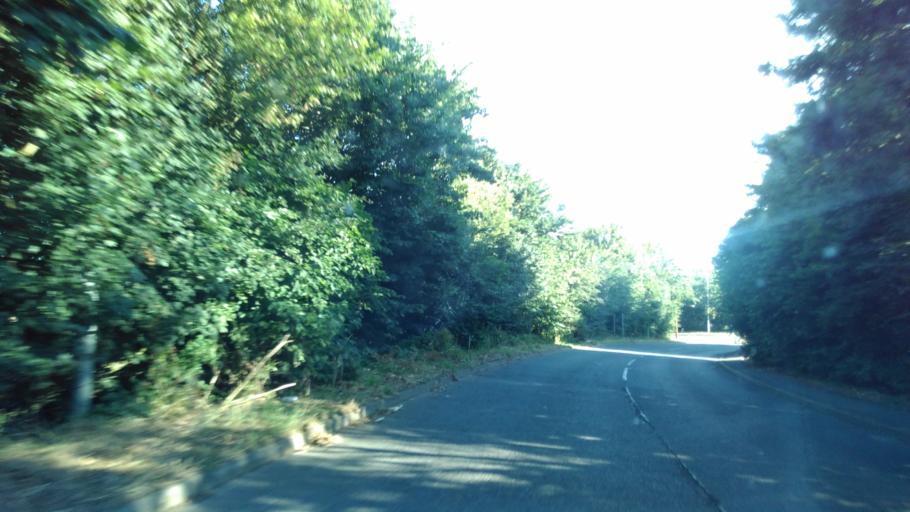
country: GB
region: England
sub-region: Kent
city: Faversham
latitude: 51.3094
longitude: 0.9322
